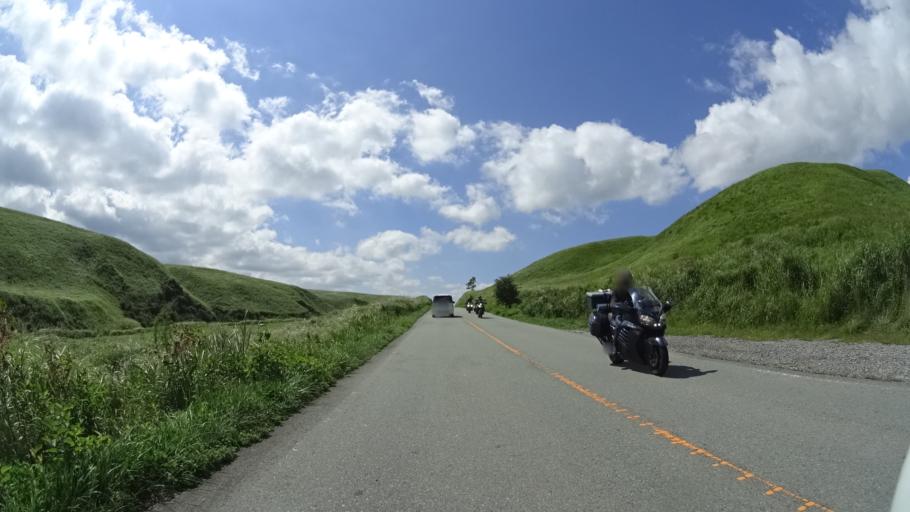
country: JP
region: Kumamoto
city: Aso
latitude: 33.0100
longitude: 131.1470
